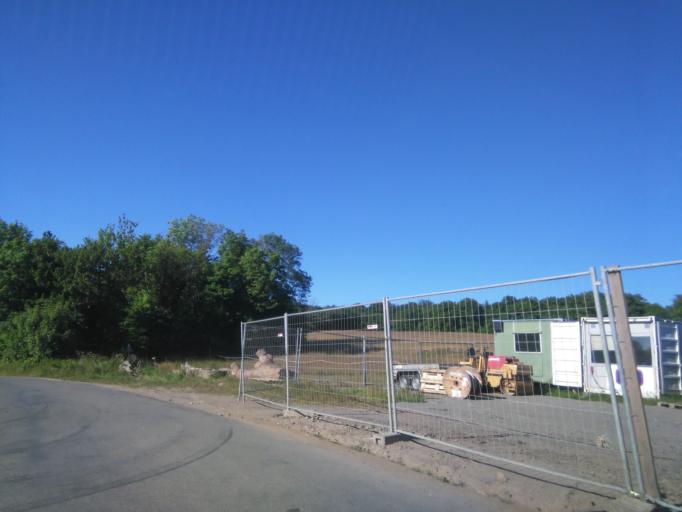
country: DK
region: Capital Region
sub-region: Bornholm Kommune
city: Ronne
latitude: 55.2714
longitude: 14.7626
